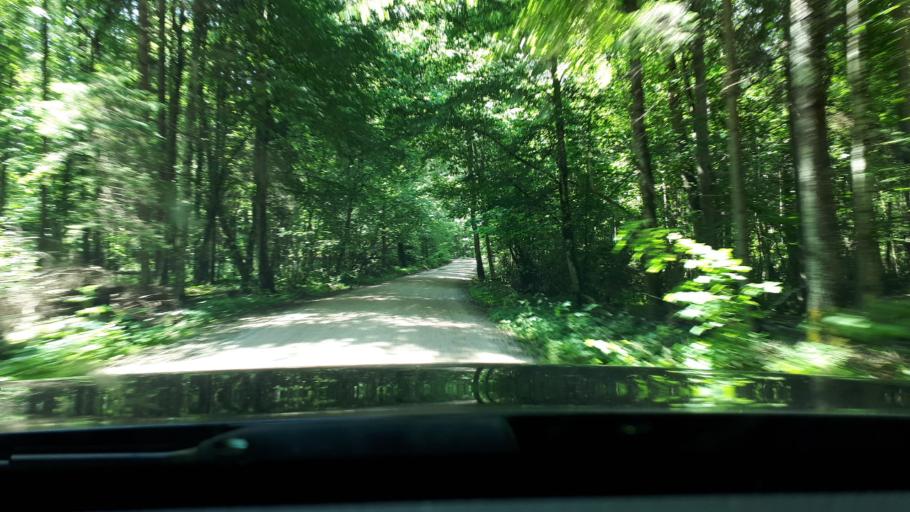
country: PL
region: Podlasie
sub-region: Powiat bialostocki
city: Suprasl
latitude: 53.2385
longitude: 23.3434
